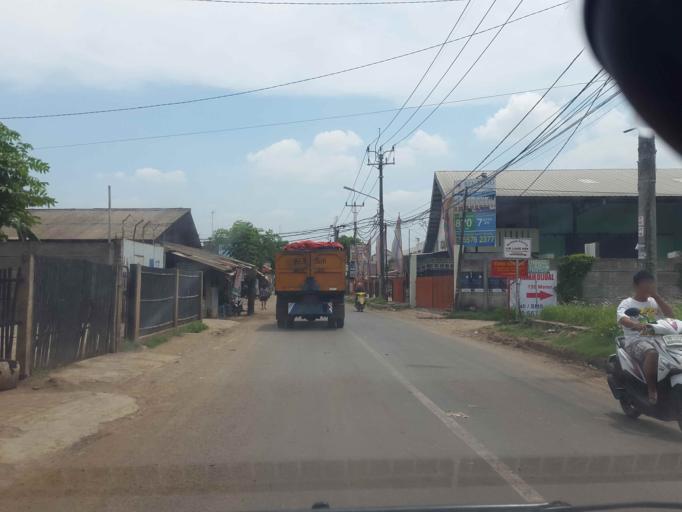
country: ID
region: Banten
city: Tangerang
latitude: -6.1457
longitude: 106.6194
